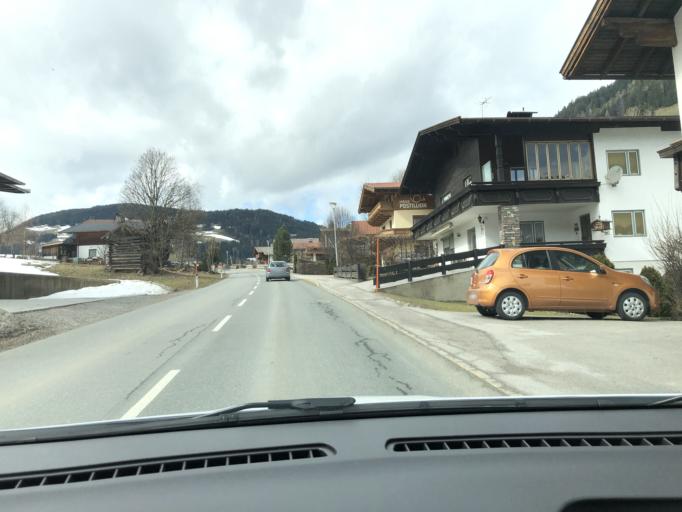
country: AT
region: Tyrol
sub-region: Politischer Bezirk Kufstein
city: Worgl
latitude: 47.4496
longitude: 12.0759
